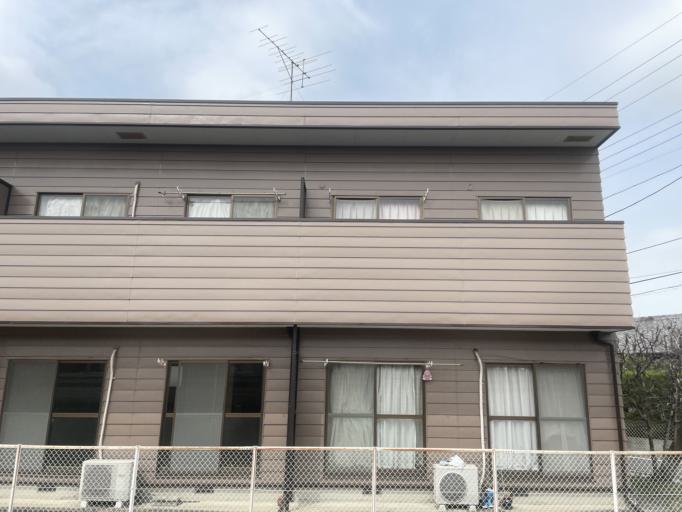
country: JP
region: Saitama
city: Gyoda
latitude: 36.1524
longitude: 139.4740
